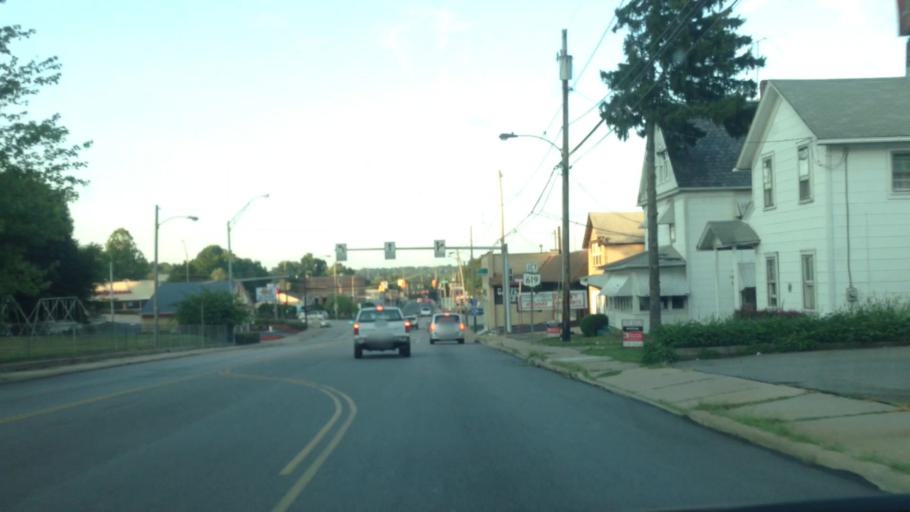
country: US
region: Ohio
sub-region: Summit County
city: Barberton
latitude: 41.0282
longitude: -81.5898
